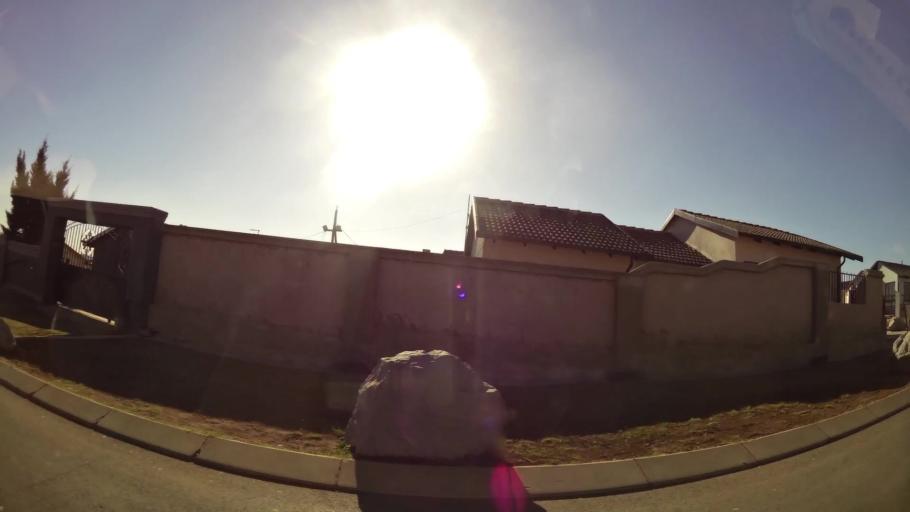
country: ZA
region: Gauteng
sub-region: Ekurhuleni Metropolitan Municipality
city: Tembisa
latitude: -26.0304
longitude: 28.2183
